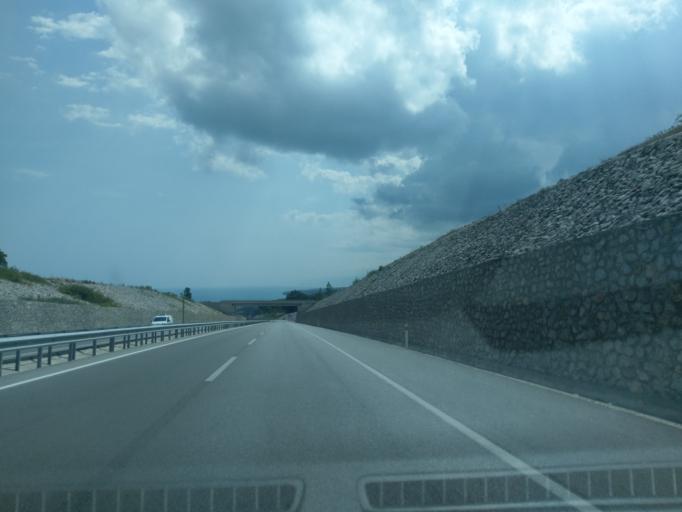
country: TR
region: Sinop
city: Kabali
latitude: 41.8516
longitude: 35.1201
